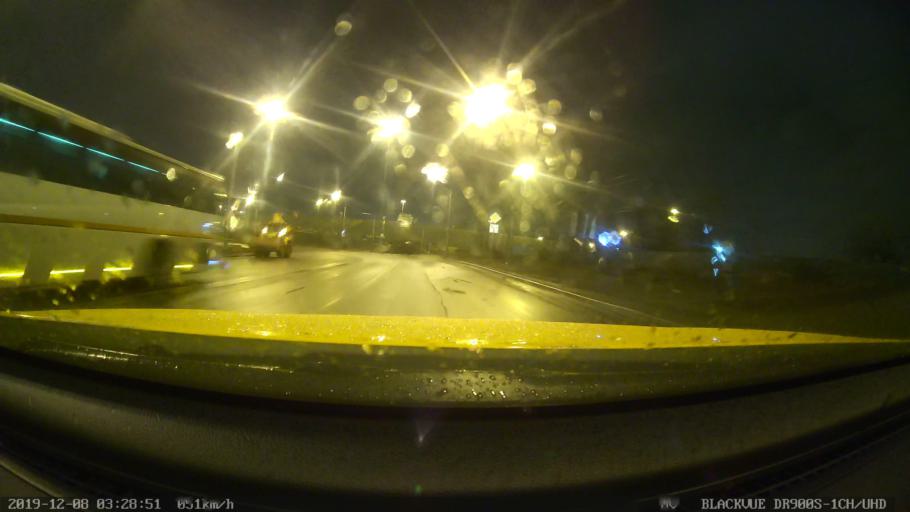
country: RU
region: Moskovskaya
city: Mosrentgen
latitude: 55.6248
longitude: 37.4265
